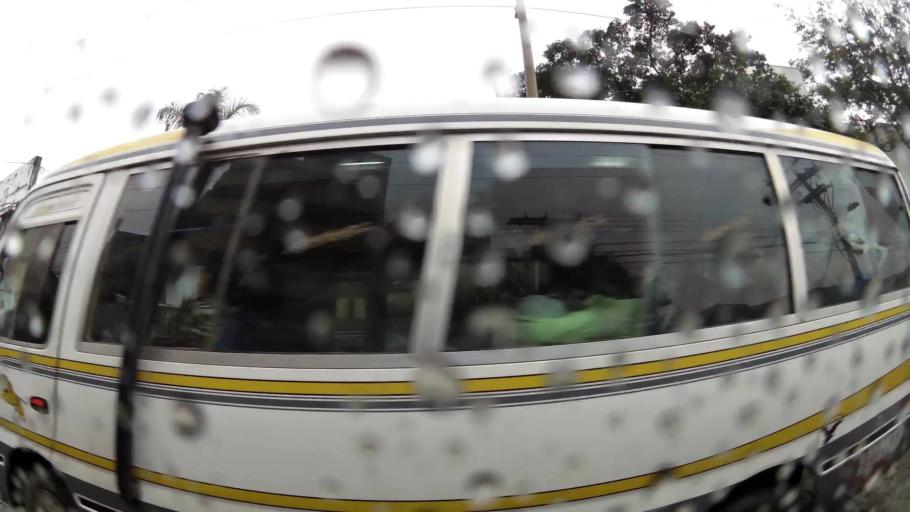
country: BO
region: Santa Cruz
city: Santa Cruz de la Sierra
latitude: -17.7770
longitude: -63.1710
